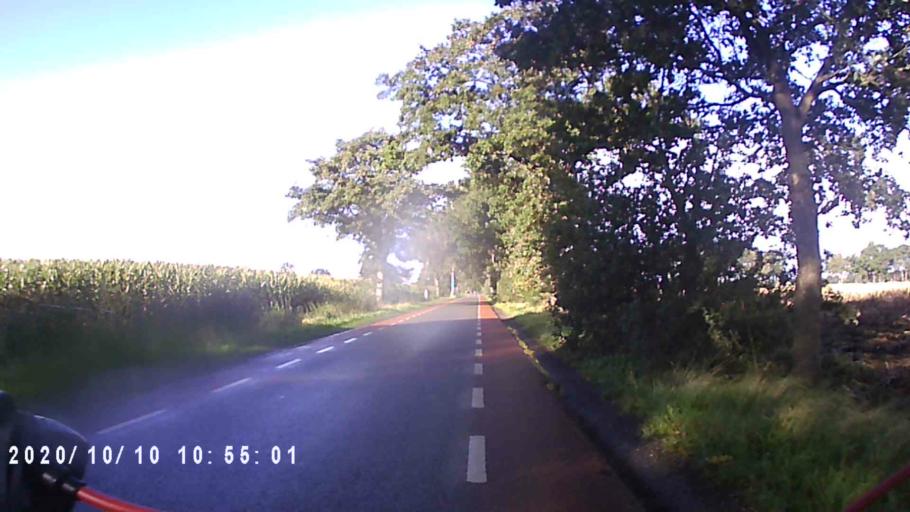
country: NL
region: Friesland
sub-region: Gemeente Achtkarspelen
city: Surhuisterveen
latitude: 53.1545
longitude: 6.2100
